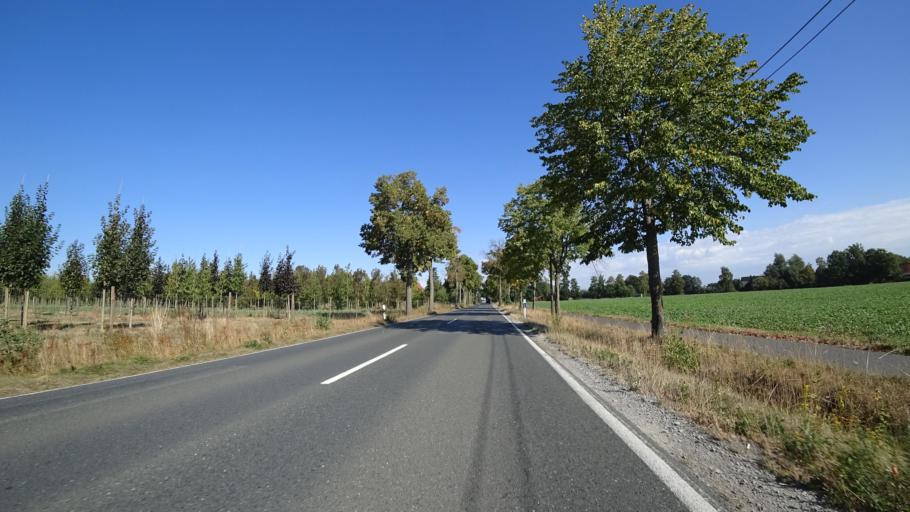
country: DE
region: North Rhine-Westphalia
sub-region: Regierungsbezirk Detmold
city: Rheda-Wiedenbruck
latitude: 51.8858
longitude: 8.2813
